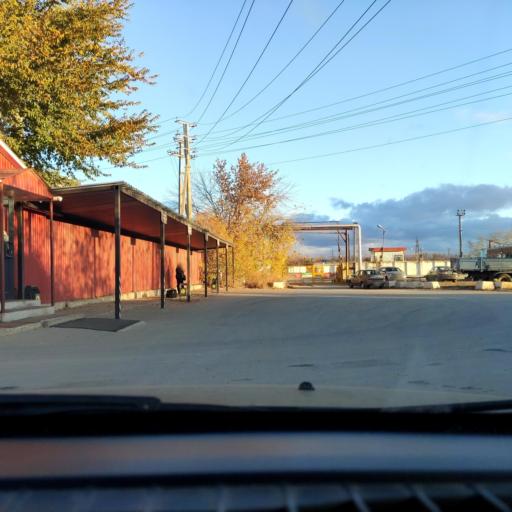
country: RU
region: Samara
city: Tol'yatti
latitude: 53.5790
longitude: 49.2635
